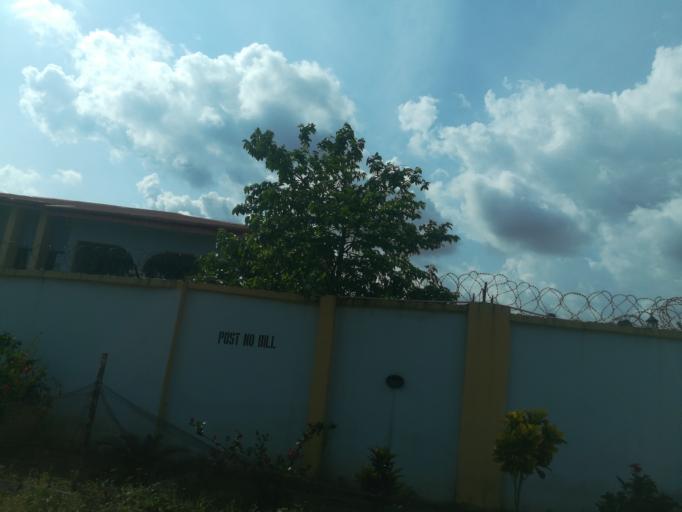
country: NG
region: Oyo
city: Ibadan
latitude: 7.3912
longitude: 3.8221
